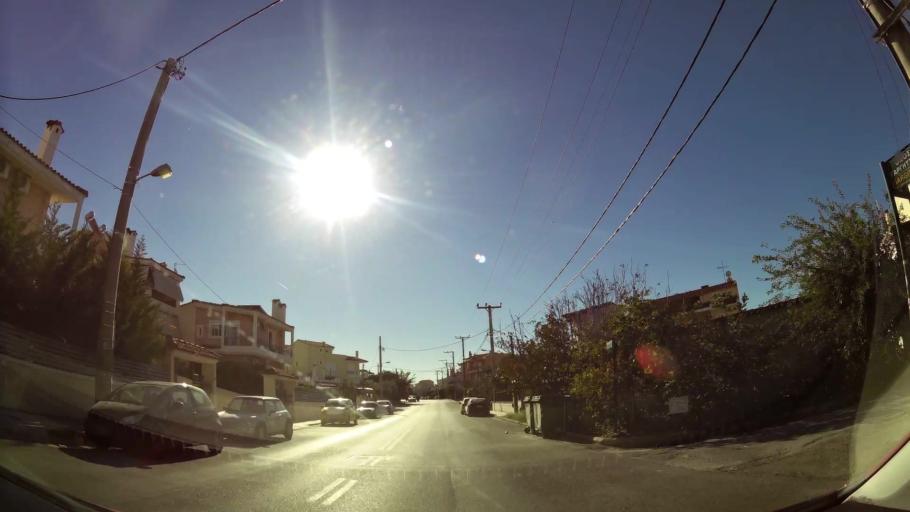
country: GR
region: Attica
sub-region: Nomarchia Anatolikis Attikis
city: Gerakas
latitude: 38.0156
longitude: 23.8545
